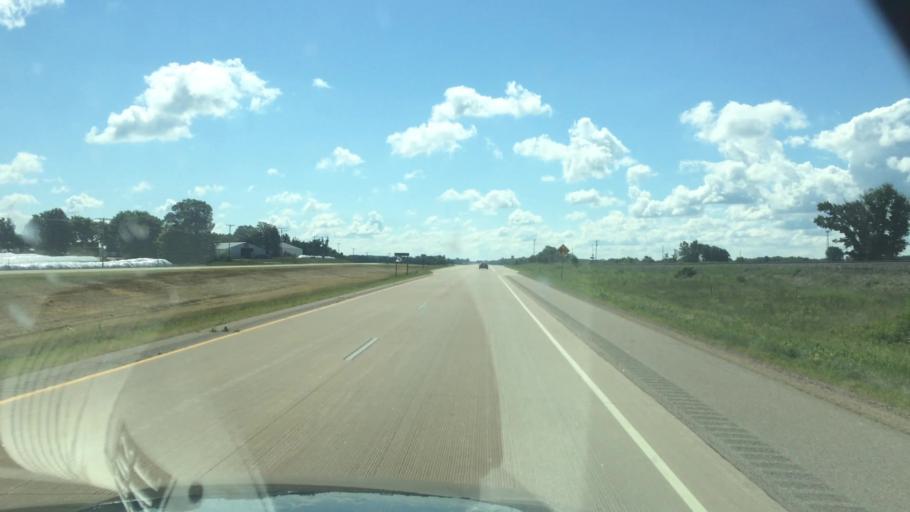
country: US
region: Wisconsin
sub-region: Portage County
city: Amherst
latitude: 44.4956
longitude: -89.3693
